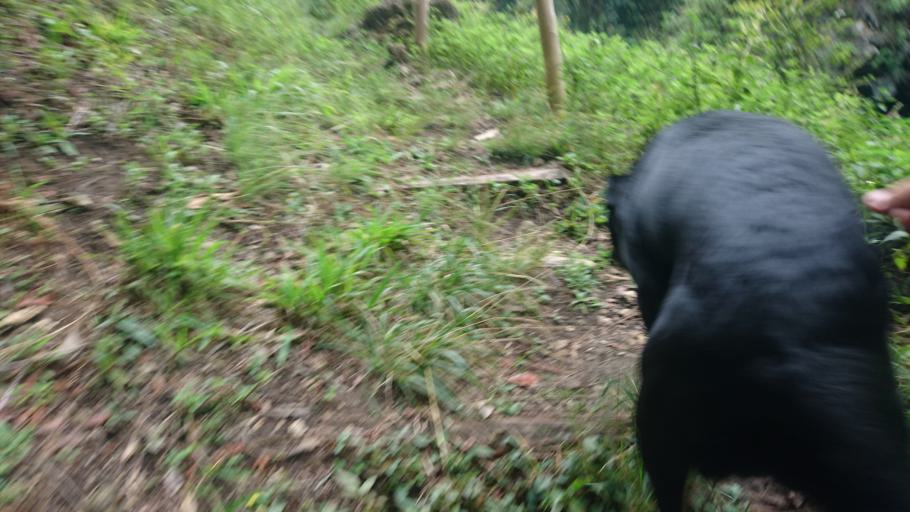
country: GT
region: Huehuetenango
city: Union
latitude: 16.1345
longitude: -91.7279
